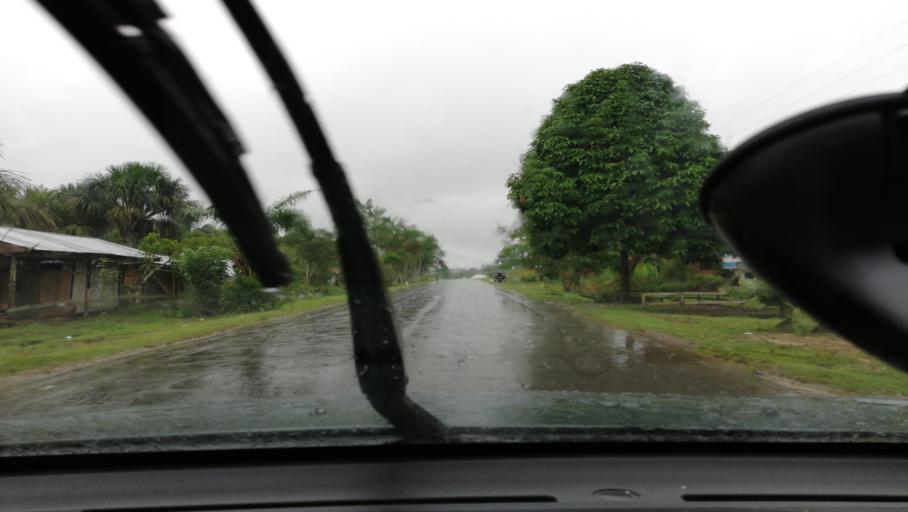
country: PE
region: Loreto
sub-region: Provincia de Maynas
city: San Juan
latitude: -4.0912
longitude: -73.4517
